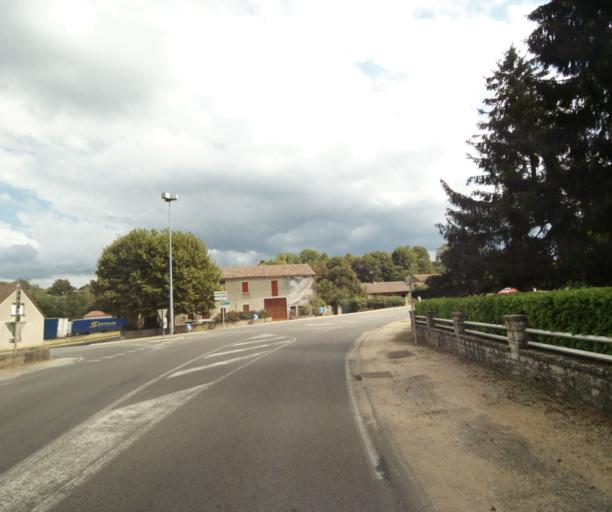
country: FR
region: Bourgogne
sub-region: Departement de Saone-et-Loire
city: Tournus
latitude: 46.5606
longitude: 4.9285
